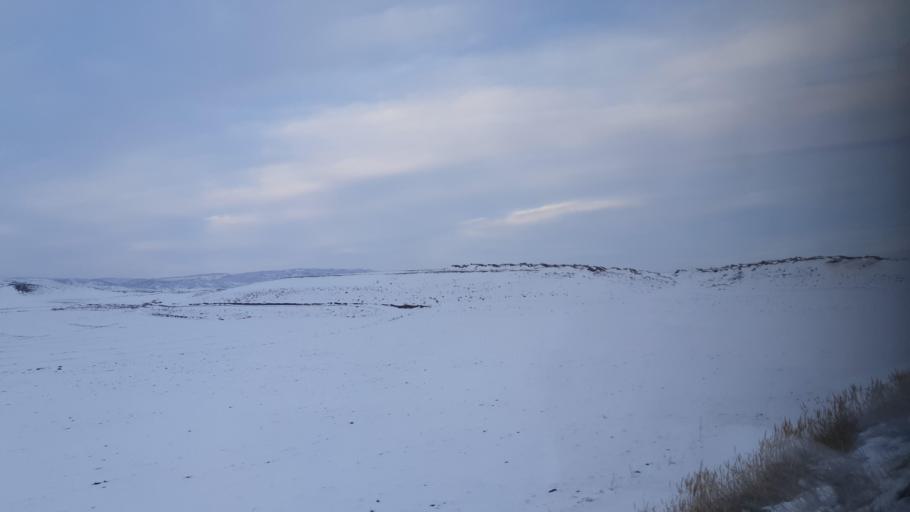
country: TR
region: Yozgat
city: Yerkoy
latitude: 39.6859
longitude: 34.4156
